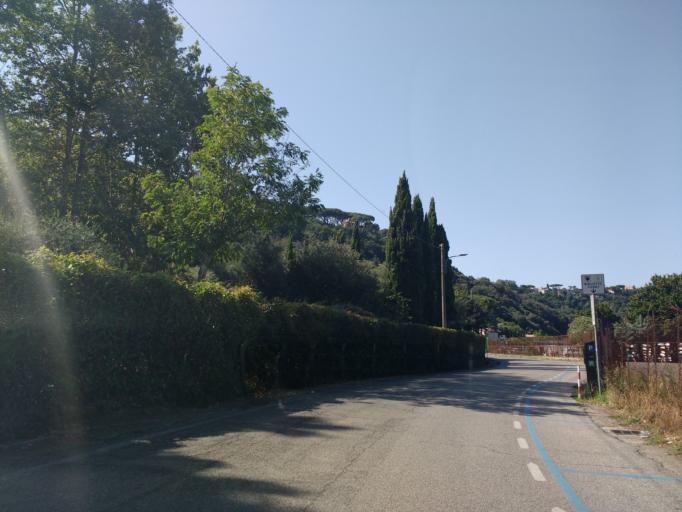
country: IT
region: Latium
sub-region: Citta metropolitana di Roma Capitale
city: Castel Gandolfo
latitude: 41.7512
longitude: 12.6518
